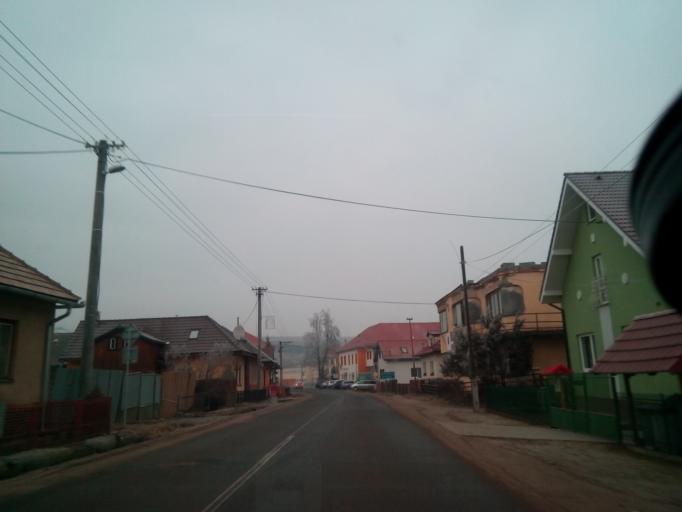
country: SK
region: Presovsky
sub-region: Okres Poprad
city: Poprad
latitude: 48.9742
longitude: 20.4081
